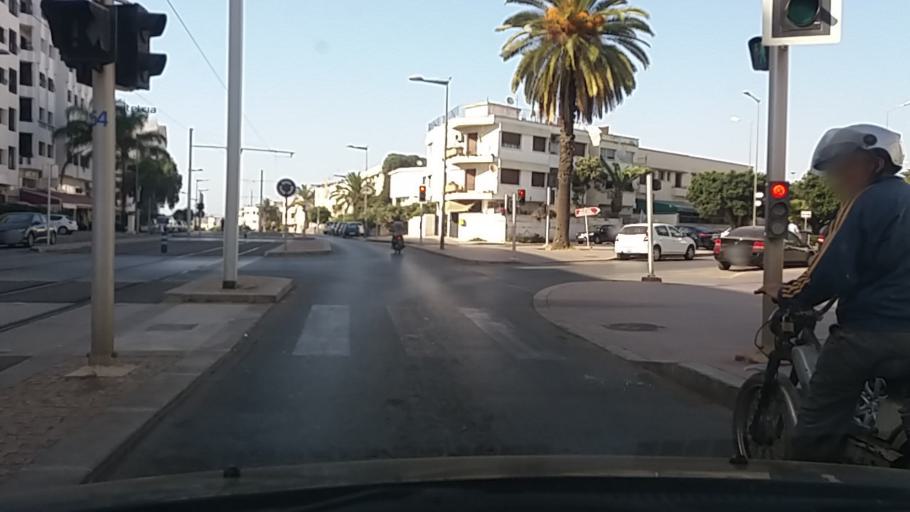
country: MA
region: Rabat-Sale-Zemmour-Zaer
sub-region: Rabat
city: Rabat
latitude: 34.0209
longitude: -6.8251
